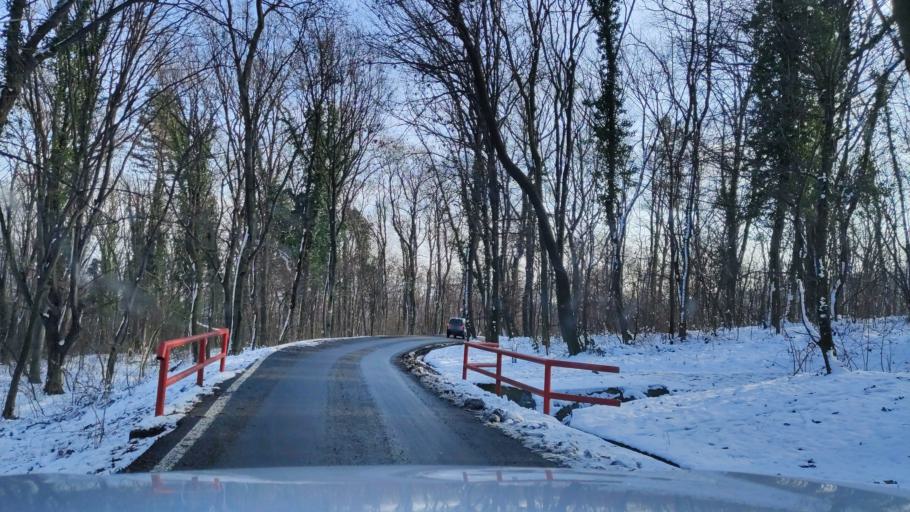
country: RS
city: Rusanj
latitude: 44.6972
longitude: 20.5163
